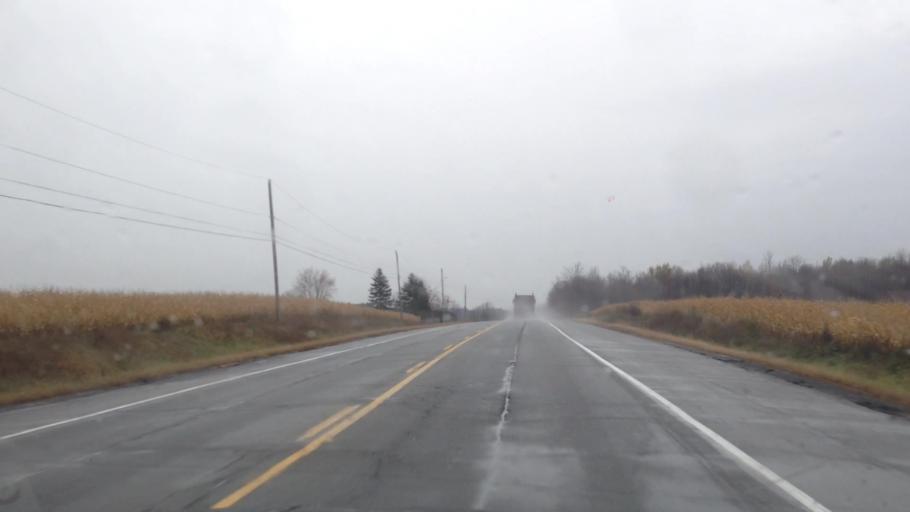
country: CA
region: Ontario
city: Clarence-Rockland
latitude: 45.3941
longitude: -75.3927
